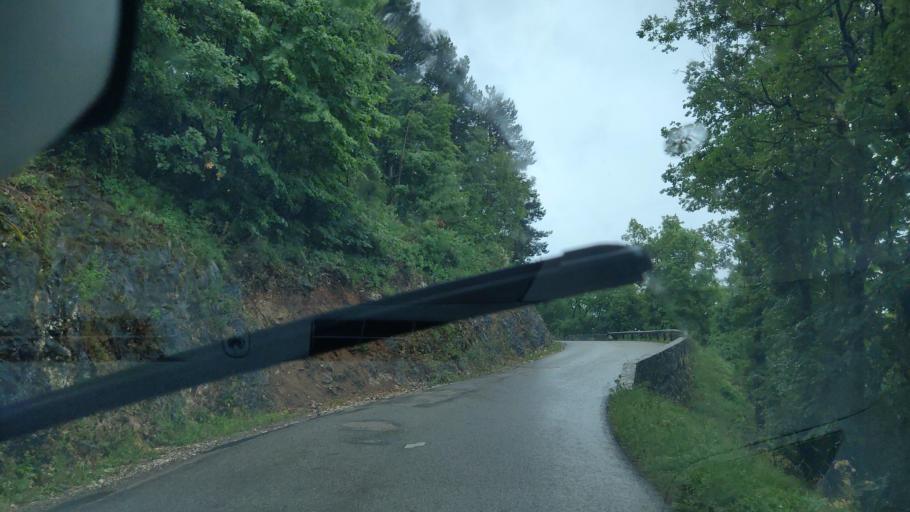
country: FR
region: Rhone-Alpes
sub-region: Departement de la Savoie
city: Chatillon
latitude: 45.7913
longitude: 5.8630
